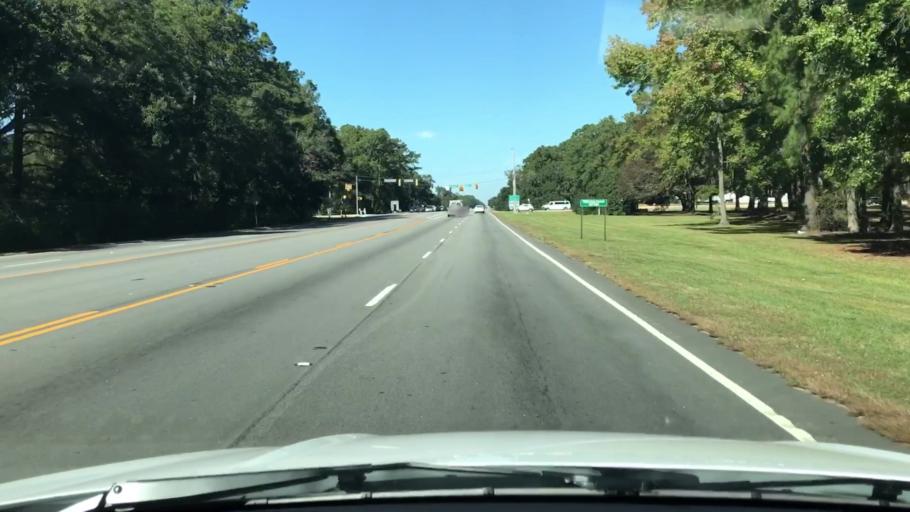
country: US
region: South Carolina
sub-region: Beaufort County
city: Burton
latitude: 32.4562
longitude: -80.7331
